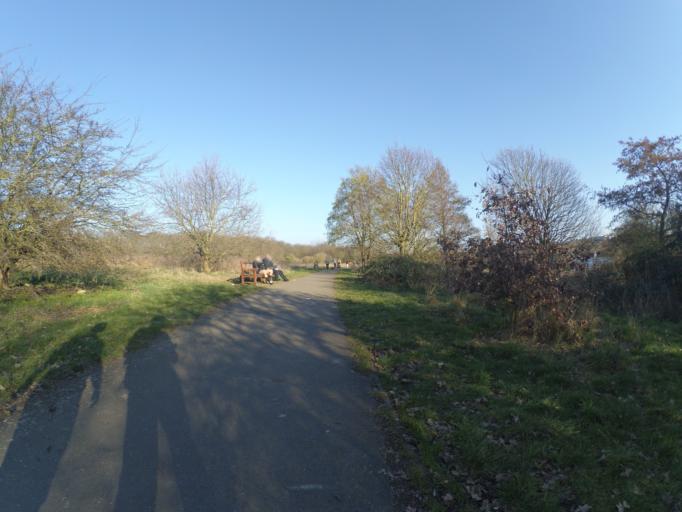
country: GB
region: England
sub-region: Greater London
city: Wembley
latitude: 51.5694
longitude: -0.2537
